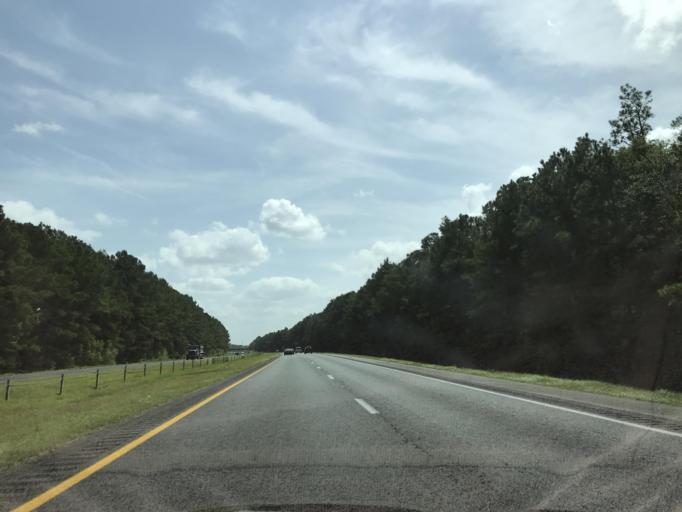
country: US
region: North Carolina
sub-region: Duplin County
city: Wallace
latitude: 34.7104
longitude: -77.9457
